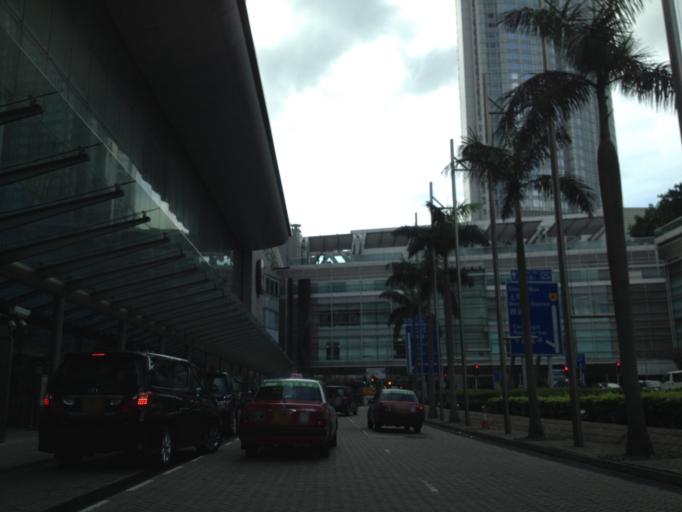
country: HK
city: Hong Kong
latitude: 22.2848
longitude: 114.1586
